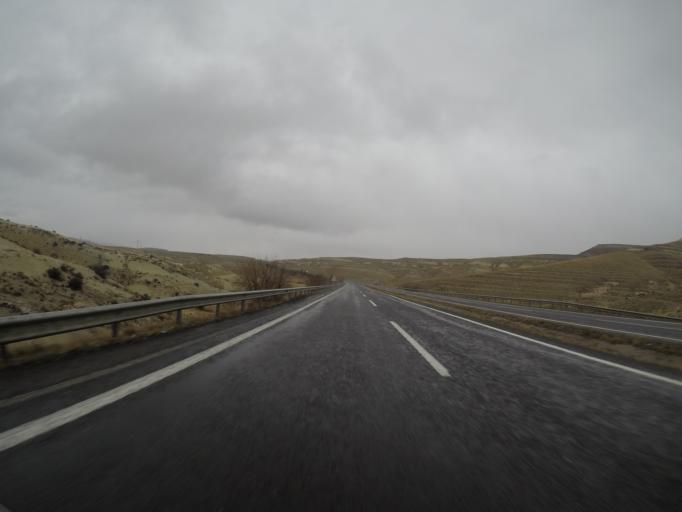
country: TR
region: Nevsehir
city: Urgub
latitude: 38.7387
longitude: 34.9930
